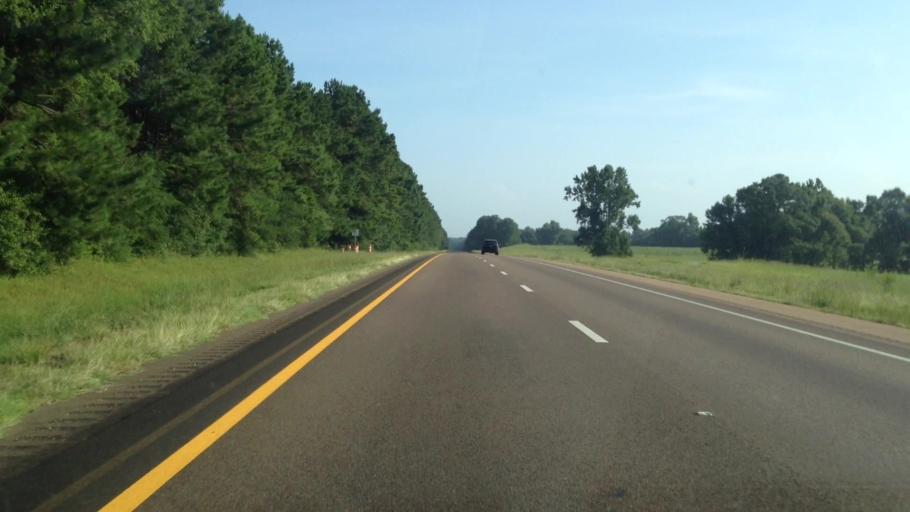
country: US
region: Mississippi
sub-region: Pike County
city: Summit
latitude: 31.3095
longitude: -90.4777
